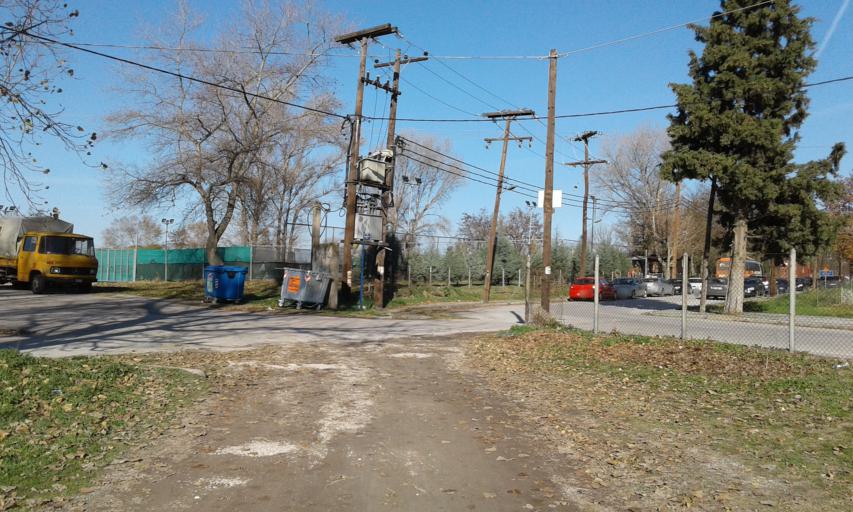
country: GR
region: Central Macedonia
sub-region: Nomos Thessalonikis
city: Lagkadas
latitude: 40.7479
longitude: 23.0600
